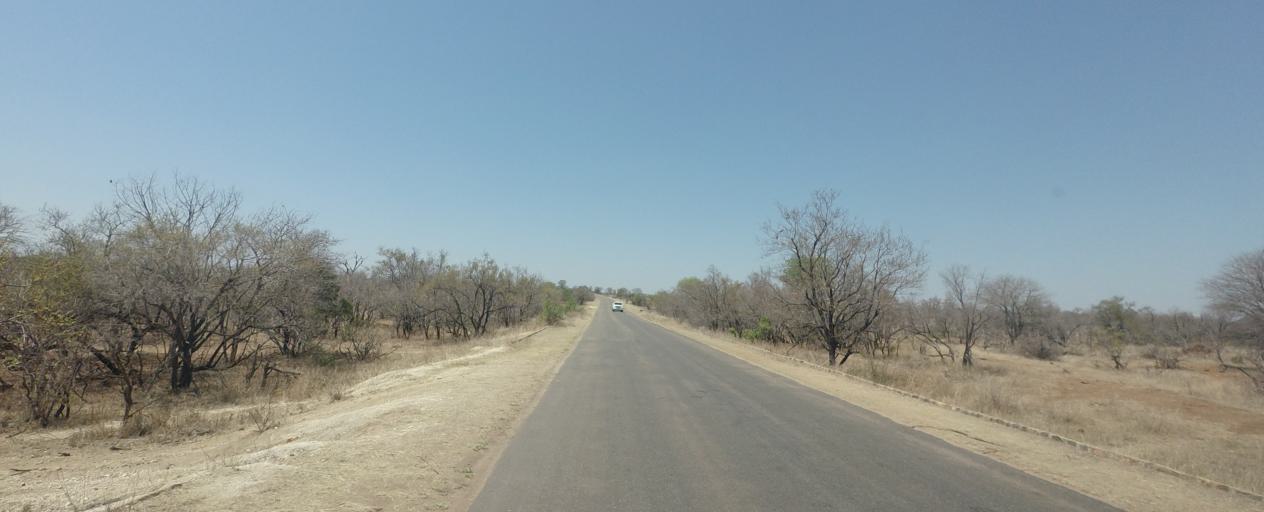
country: ZA
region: Limpopo
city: Thulamahashi
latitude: -24.4758
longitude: 31.3927
